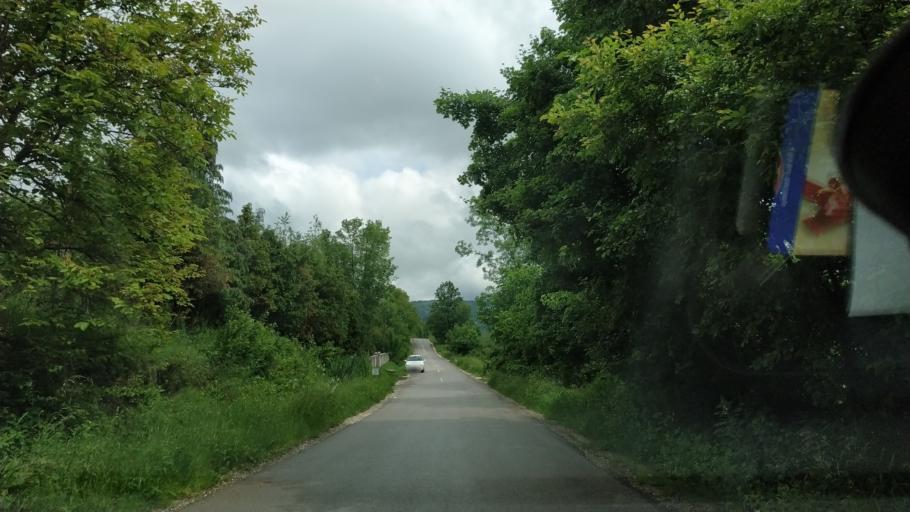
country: RS
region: Central Serbia
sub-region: Zajecarski Okrug
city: Soko Banja
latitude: 43.6537
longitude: 21.9034
